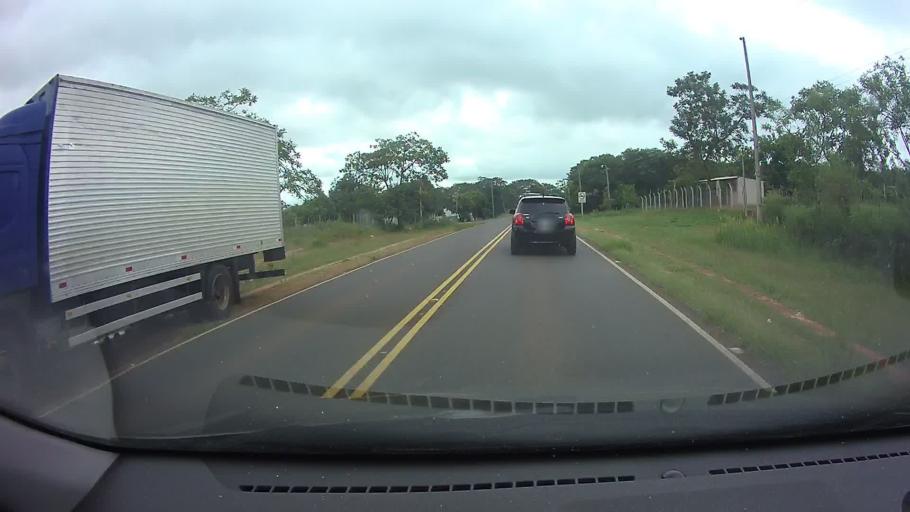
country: PY
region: Paraguari
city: Carapegua
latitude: -25.7387
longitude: -57.2878
